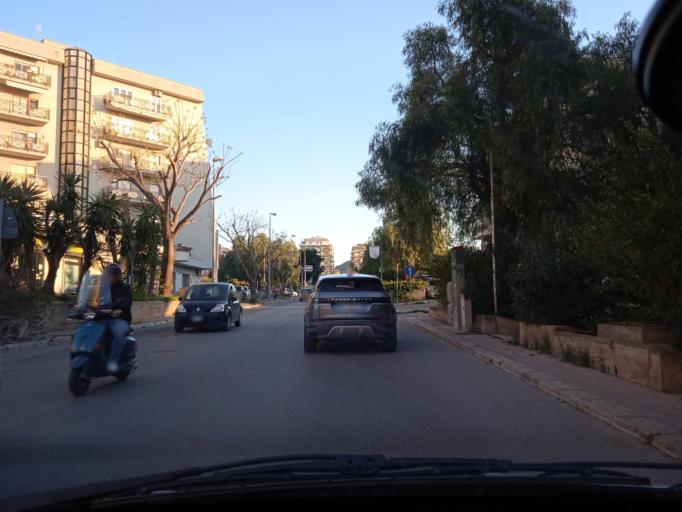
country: IT
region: Sicily
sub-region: Palermo
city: Bagheria
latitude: 38.0829
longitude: 13.5015
